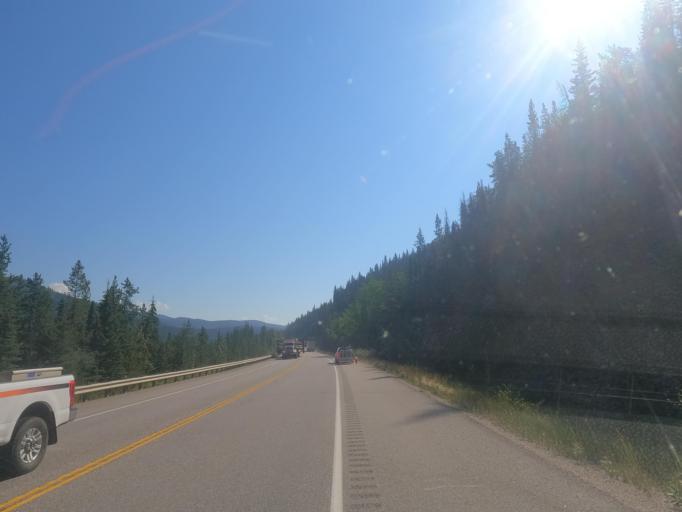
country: CA
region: Alberta
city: Jasper Park Lodge
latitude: 52.8728
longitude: -118.3007
